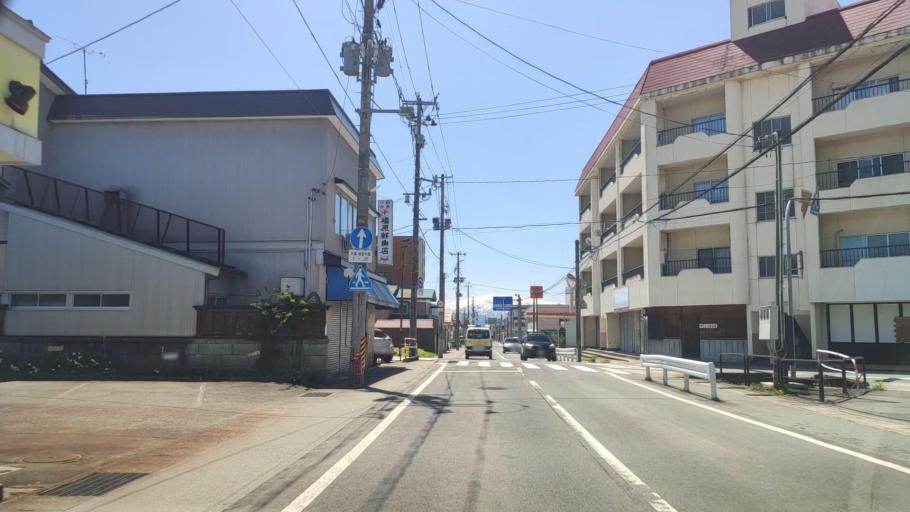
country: JP
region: Yamagata
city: Shinjo
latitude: 38.7608
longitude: 140.3019
